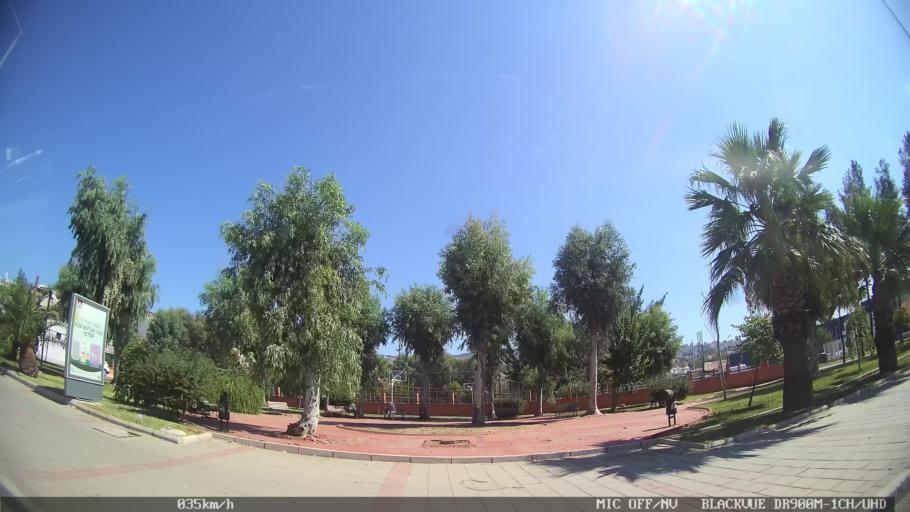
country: TR
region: Izmir
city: Karsiyaka
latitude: 38.4895
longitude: 27.0699
